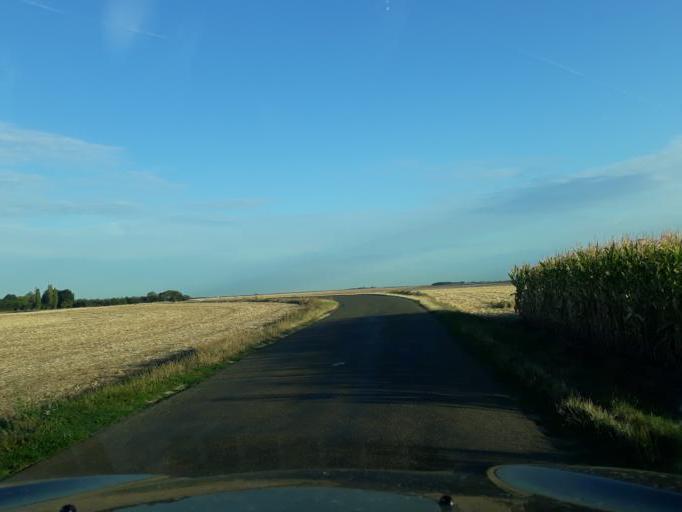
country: FR
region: Centre
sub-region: Departement du Loiret
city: Epieds-en-Beauce
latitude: 47.9390
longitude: 1.5793
